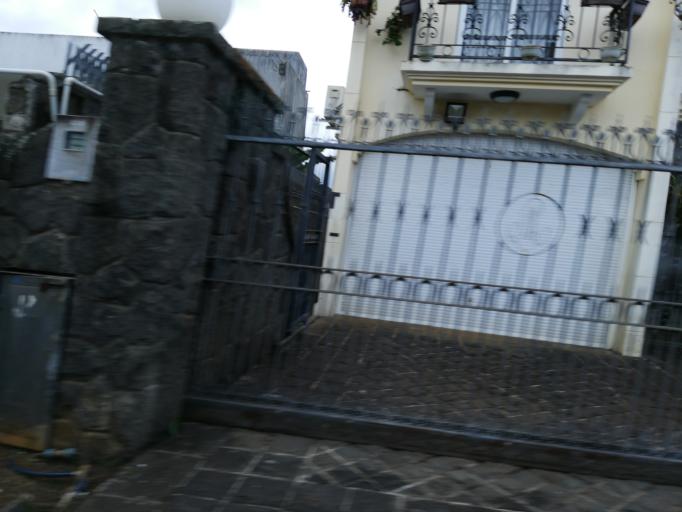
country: MU
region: Black River
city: Gros Cailloux
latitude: -20.2347
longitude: 57.4552
